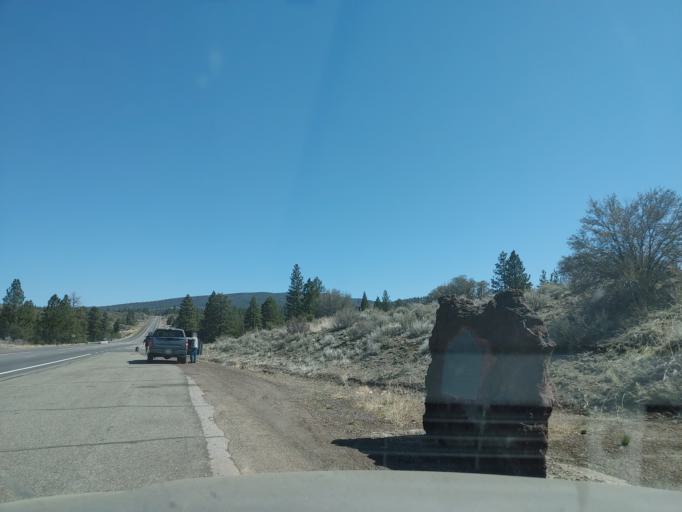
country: US
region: California
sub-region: Siskiyou County
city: Weed
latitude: 41.5584
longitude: -122.2098
